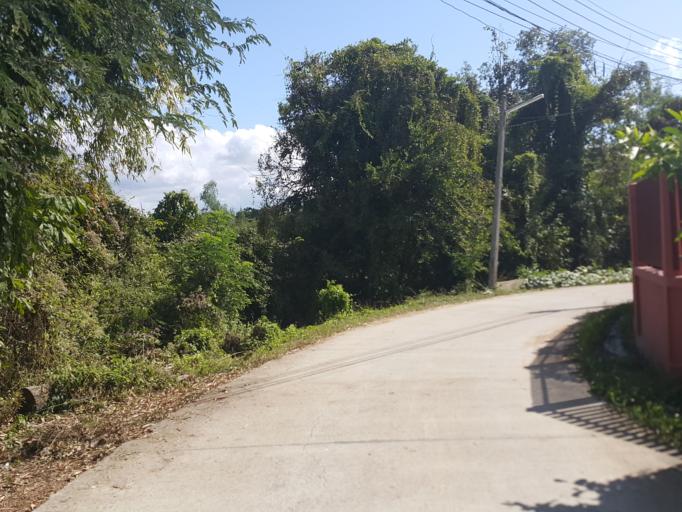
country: TH
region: Chiang Mai
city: San Kamphaeng
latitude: 18.7767
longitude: 99.1162
